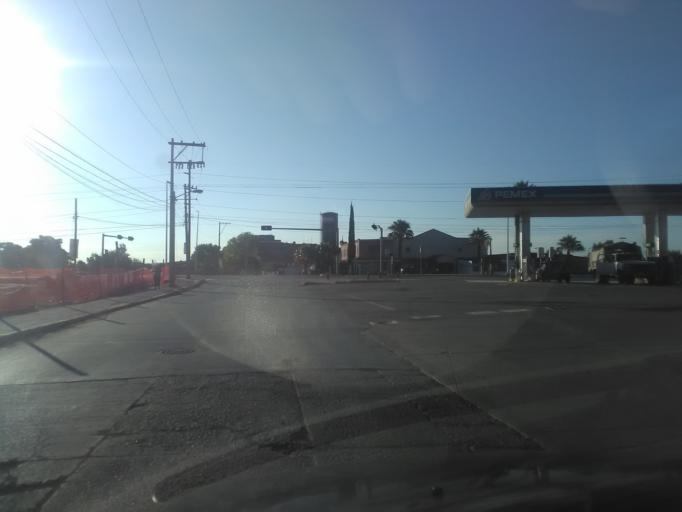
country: MX
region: Durango
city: Victoria de Durango
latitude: 24.0001
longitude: -104.7006
